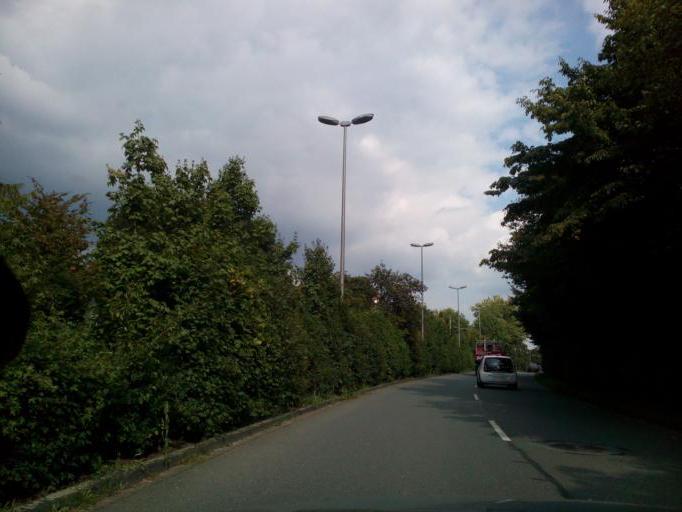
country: DE
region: North Rhine-Westphalia
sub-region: Regierungsbezirk Munster
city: Muenster
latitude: 51.9251
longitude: 7.6217
